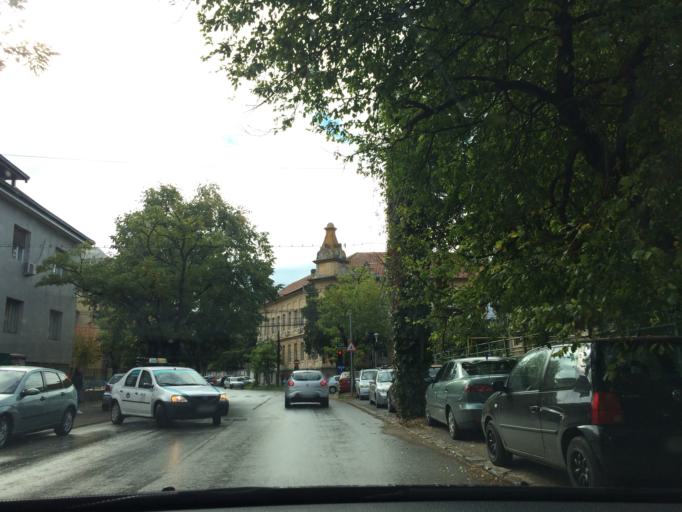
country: RO
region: Timis
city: Timisoara
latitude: 45.7450
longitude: 21.2297
